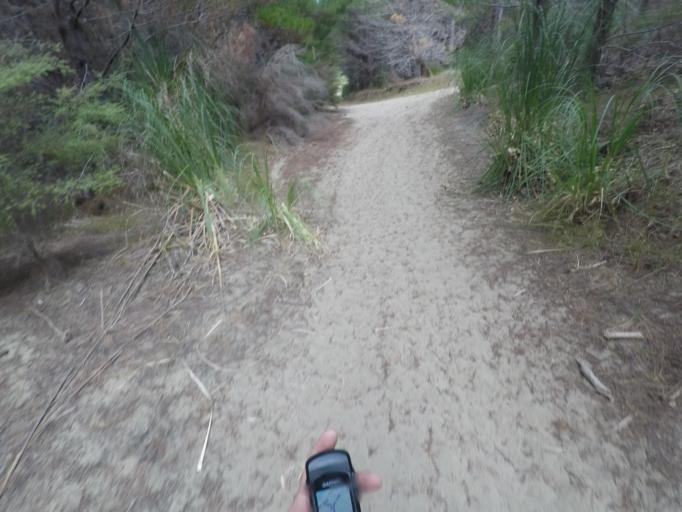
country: NZ
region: Auckland
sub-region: Auckland
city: Parakai
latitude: -36.6013
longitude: 174.2832
